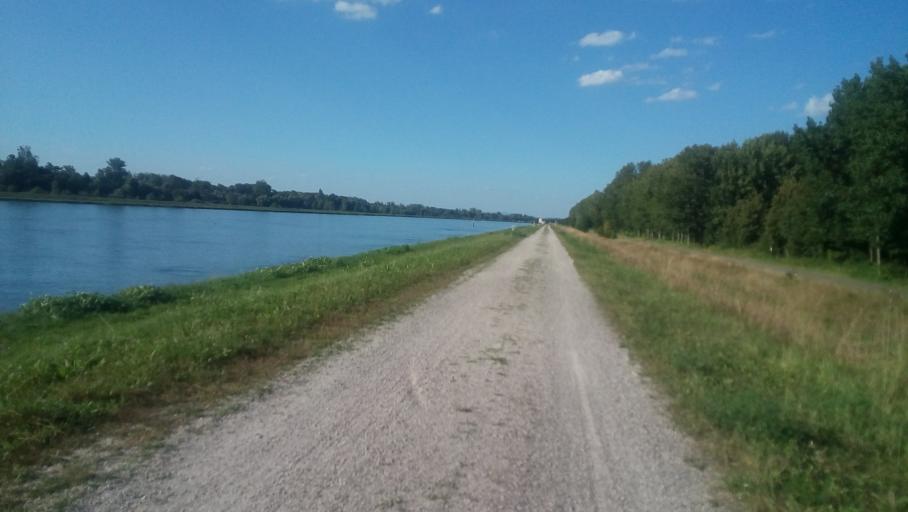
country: DE
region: Baden-Wuerttemberg
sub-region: Karlsruhe Region
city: Lichtenau
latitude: 48.7318
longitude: 7.9696
